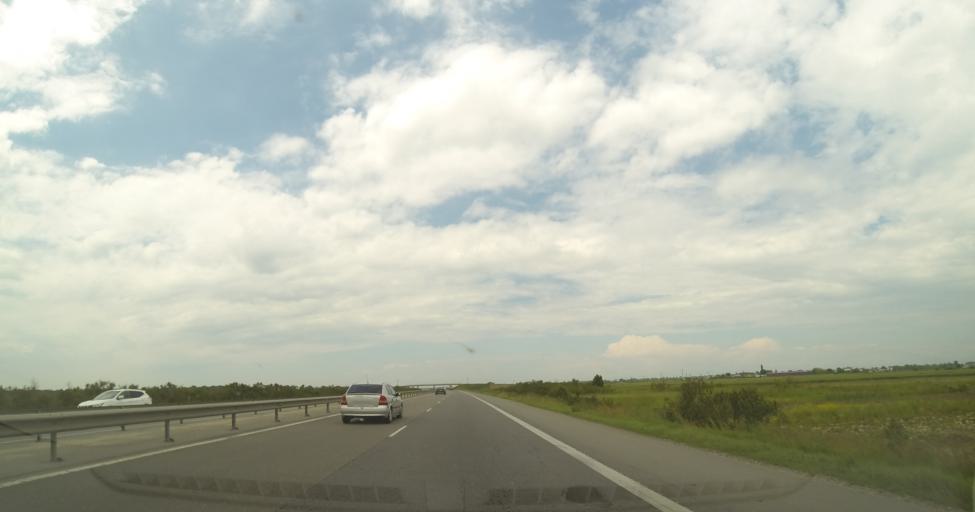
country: RO
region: Dambovita
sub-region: Comuna Corbii Mari
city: Corbii Mari
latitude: 44.5597
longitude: 25.4962
